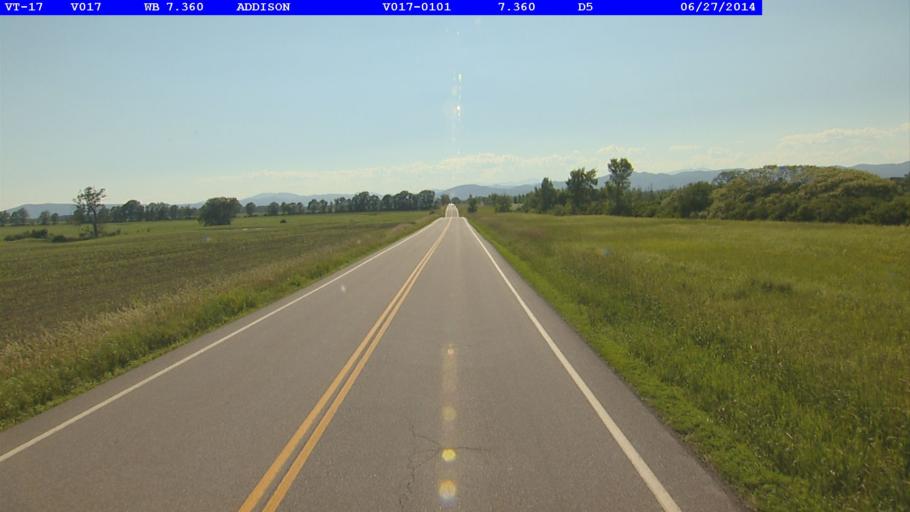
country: US
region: Vermont
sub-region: Addison County
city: Vergennes
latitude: 44.0872
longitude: -73.3227
